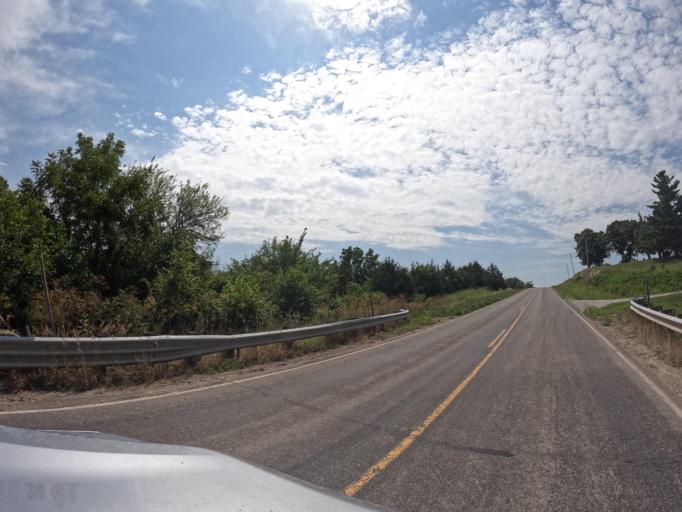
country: US
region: Iowa
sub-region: Appanoose County
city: Centerville
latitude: 40.7956
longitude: -92.9447
